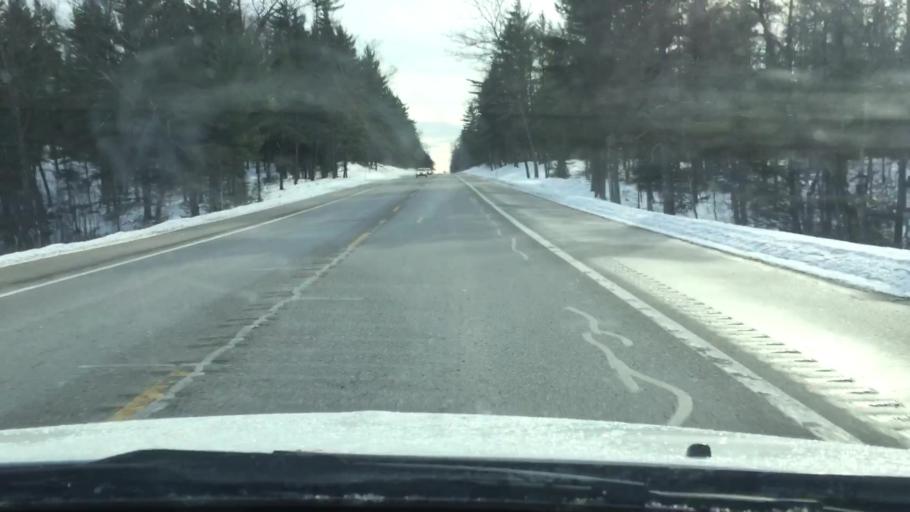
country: US
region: Michigan
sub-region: Wexford County
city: Manton
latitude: 44.5623
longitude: -85.3672
